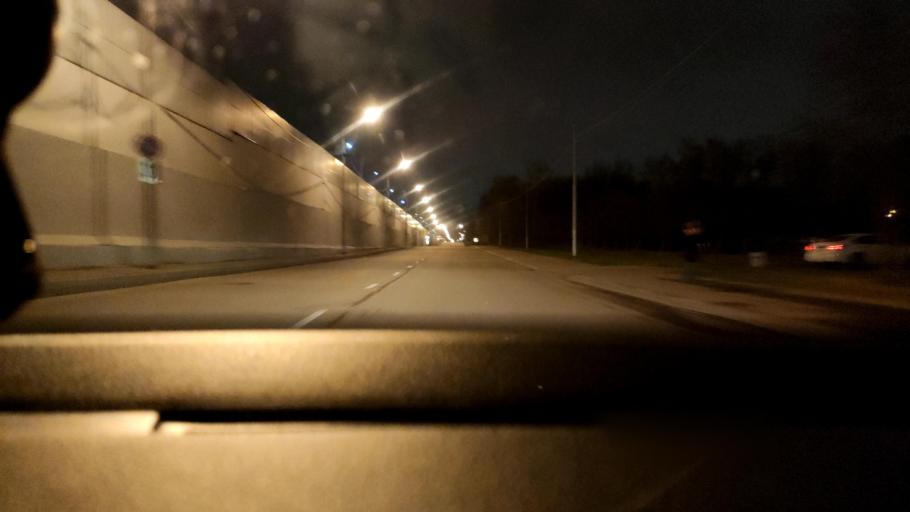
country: RU
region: Moskovskaya
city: Pavshino
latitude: 55.8580
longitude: 37.3567
